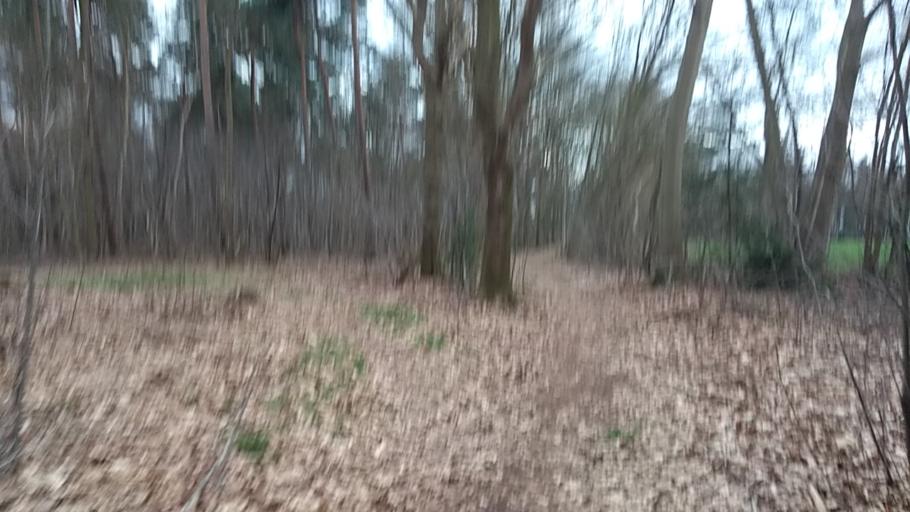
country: NL
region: Overijssel
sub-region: Gemeente Borne
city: Borne
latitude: 52.3522
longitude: 6.7204
